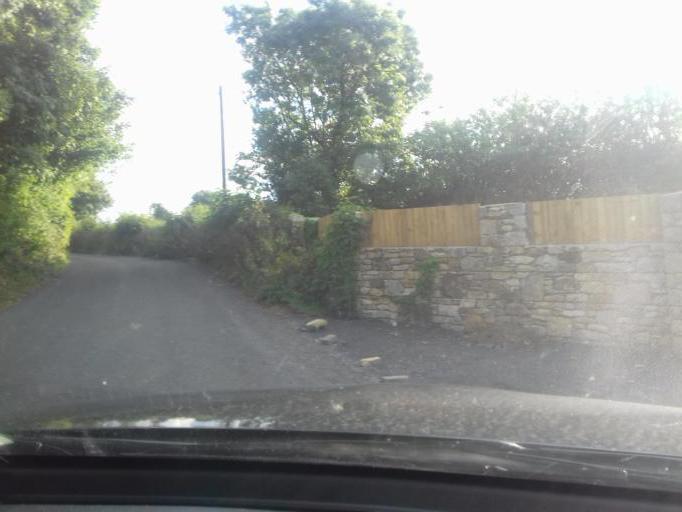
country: IE
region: Leinster
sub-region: Kilkenny
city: Graiguenamanagh
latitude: 52.5897
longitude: -6.9947
